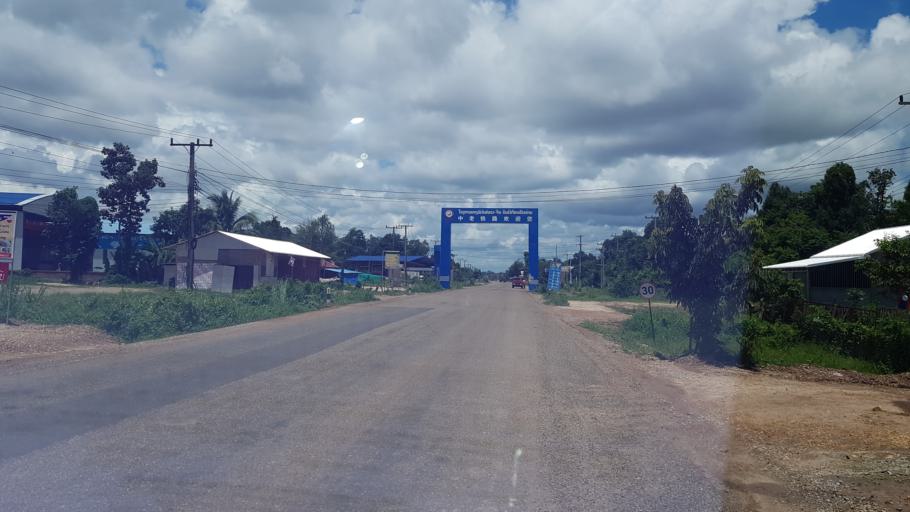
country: LA
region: Vientiane
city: Vientiane
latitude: 18.1021
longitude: 102.5607
